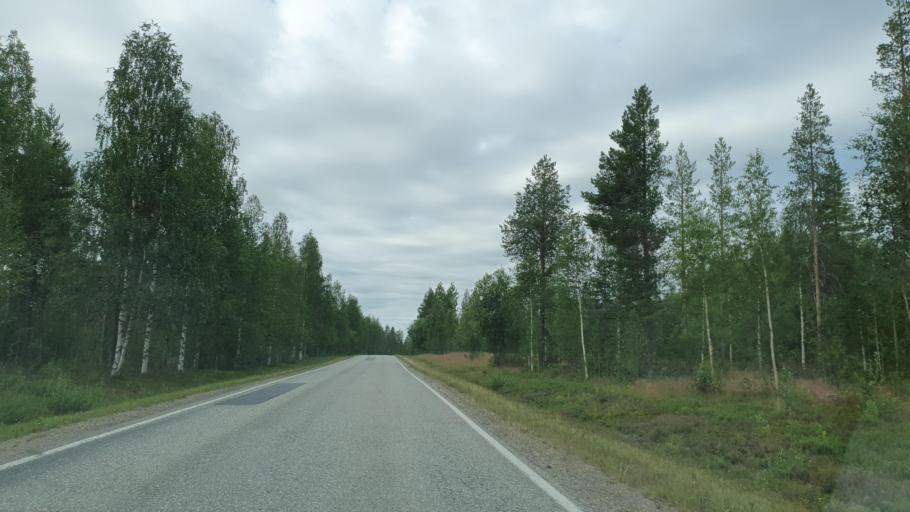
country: FI
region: Lapland
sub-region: Tunturi-Lappi
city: Kittilae
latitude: 67.6090
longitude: 25.2823
